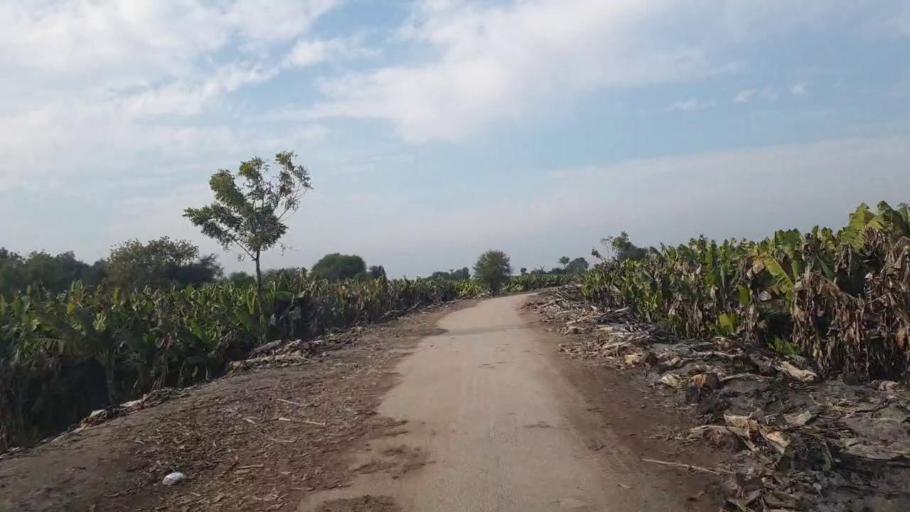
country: PK
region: Sindh
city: Shahdadpur
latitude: 26.0164
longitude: 68.5248
